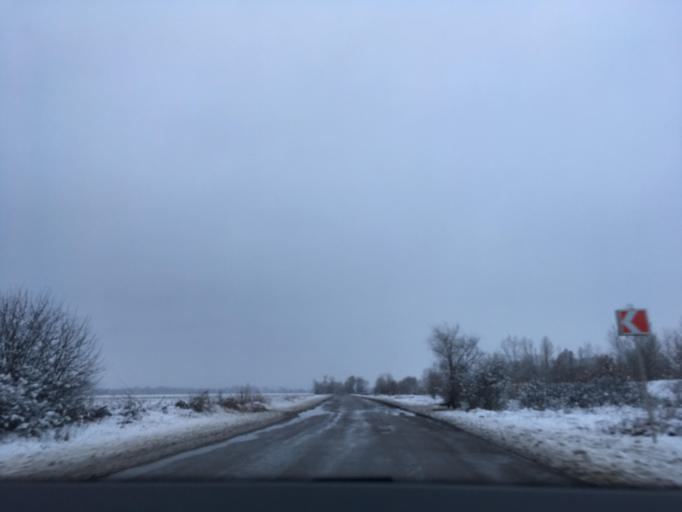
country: RU
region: Voronezj
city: Mitrofanovka
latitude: 50.1280
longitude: 39.9951
